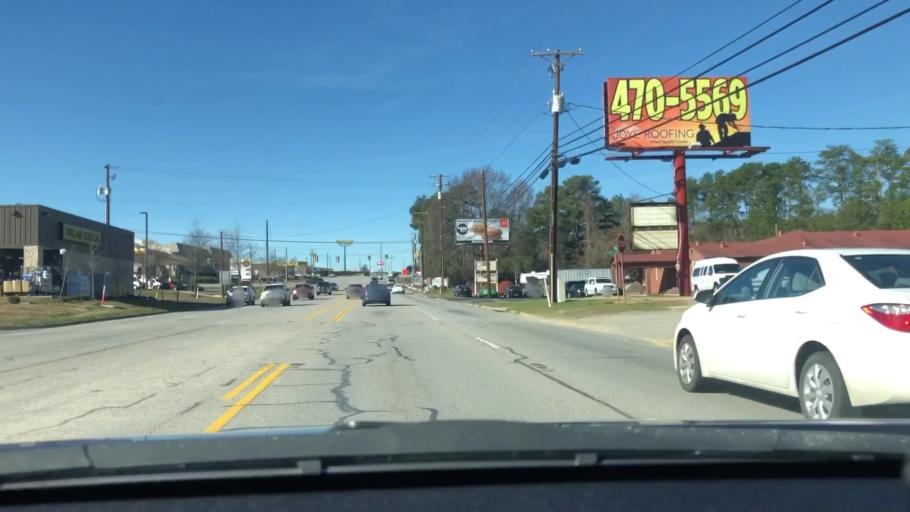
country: US
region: South Carolina
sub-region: Lexington County
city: Oak Grove
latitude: 34.0080
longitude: -81.1400
